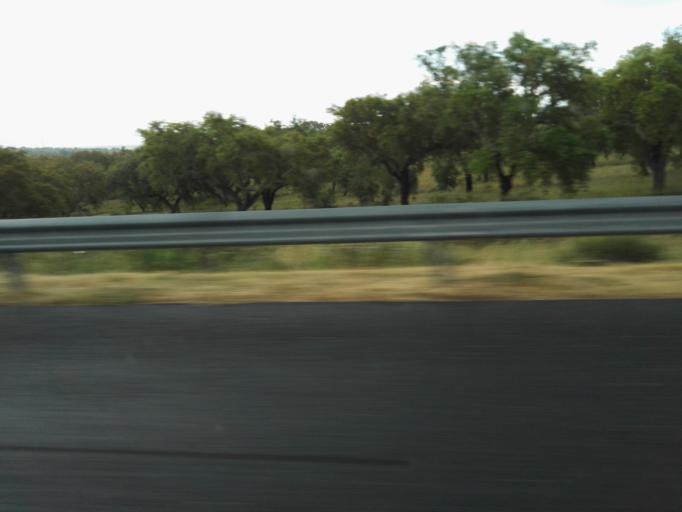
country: PT
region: Evora
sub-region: Evora
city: Evora
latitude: 38.7018
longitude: -7.8027
